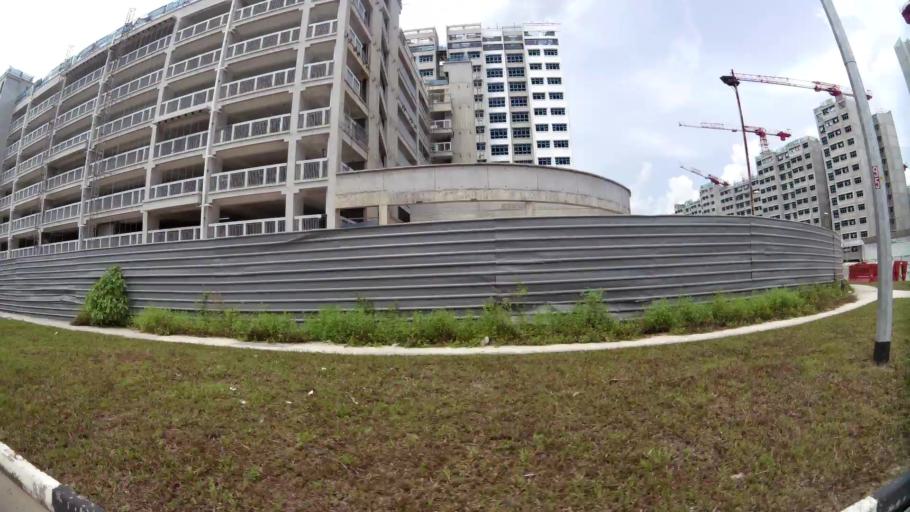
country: MY
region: Johor
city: Johor Bahru
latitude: 1.3560
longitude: 103.7396
